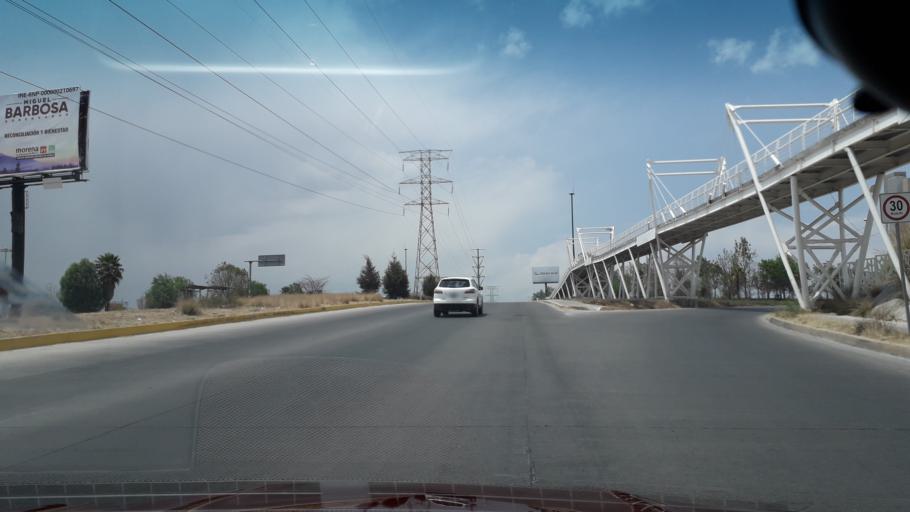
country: MX
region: Puebla
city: Tlazcalancingo
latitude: 19.0169
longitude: -98.2480
